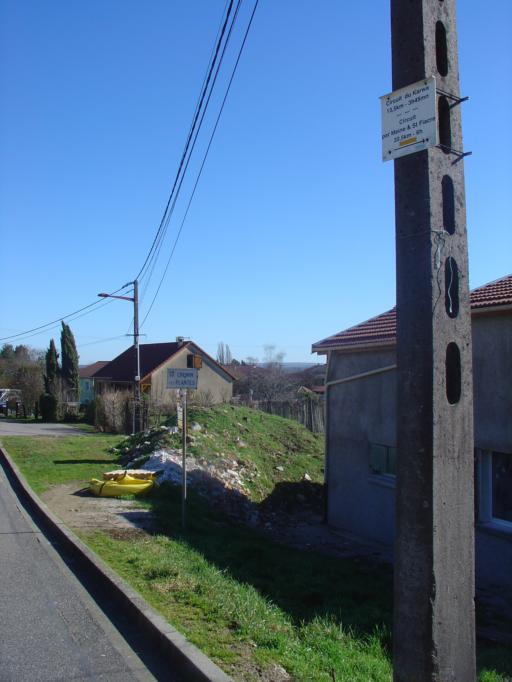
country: FR
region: Lorraine
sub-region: Departement de Meurthe-et-Moselle
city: Blenod-les-Toul
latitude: 48.5994
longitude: 5.8367
